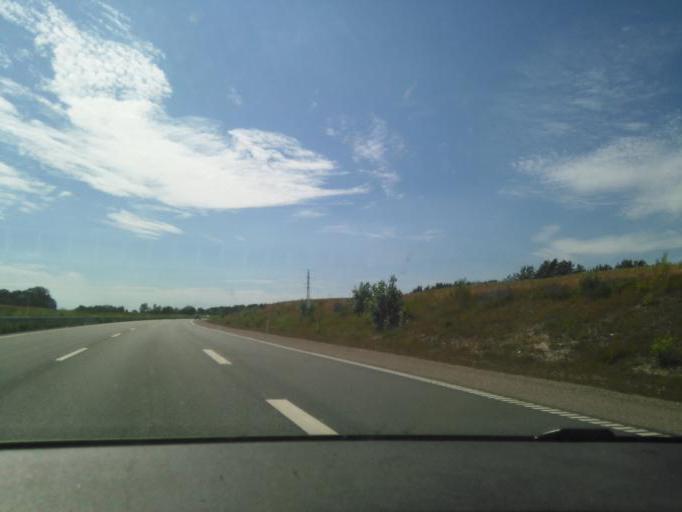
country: DK
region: Zealand
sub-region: Holbaek Kommune
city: Vipperod
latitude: 55.6467
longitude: 11.7618
